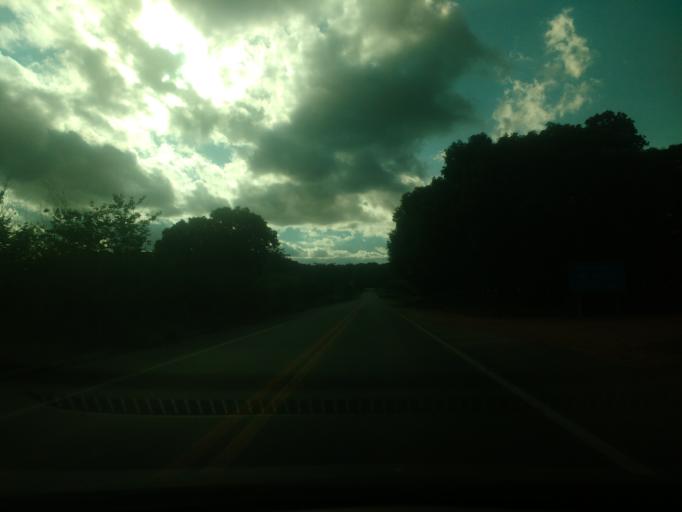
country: BR
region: Alagoas
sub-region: Murici
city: Murici
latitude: -9.3330
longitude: -35.8968
